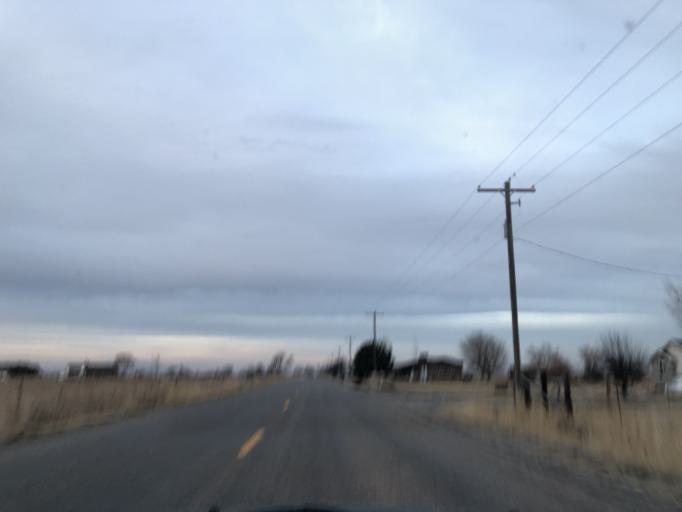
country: US
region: Utah
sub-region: Cache County
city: Benson
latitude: 41.7779
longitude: -111.9123
